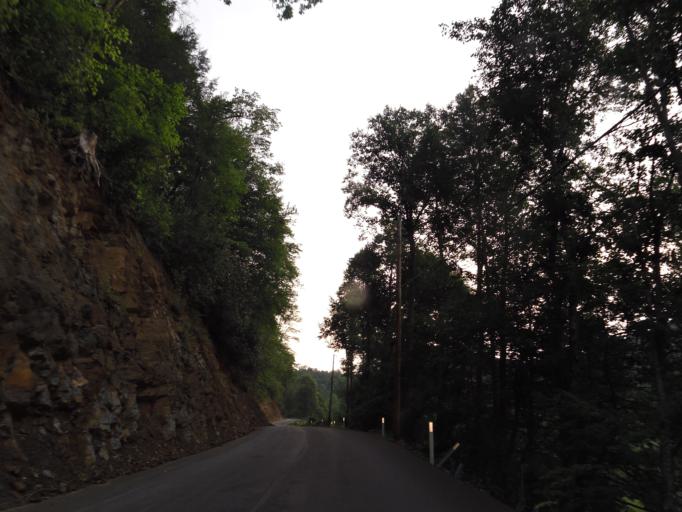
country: US
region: Tennessee
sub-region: Sevier County
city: Seymour
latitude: 35.7546
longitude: -83.7227
